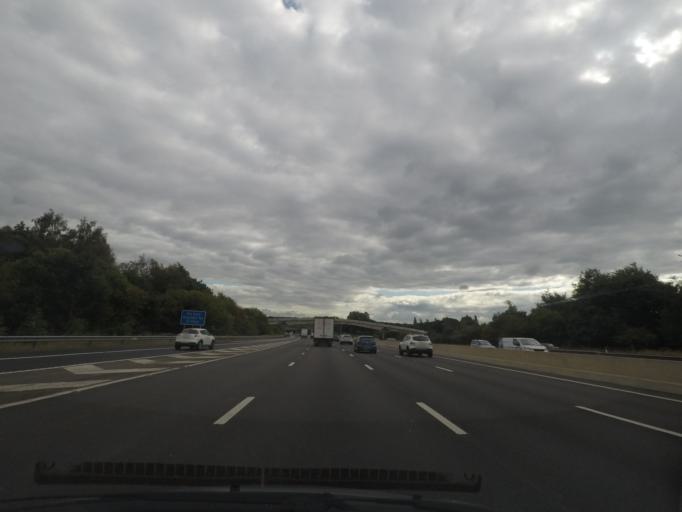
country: GB
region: England
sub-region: Sheffield
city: Chapletown
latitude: 53.4513
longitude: -1.4447
